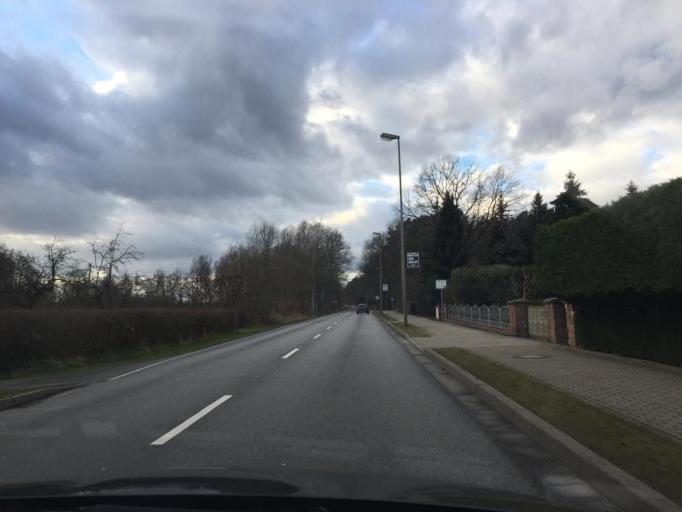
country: DE
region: Brandenburg
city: Kolkwitz
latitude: 51.7501
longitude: 14.2355
